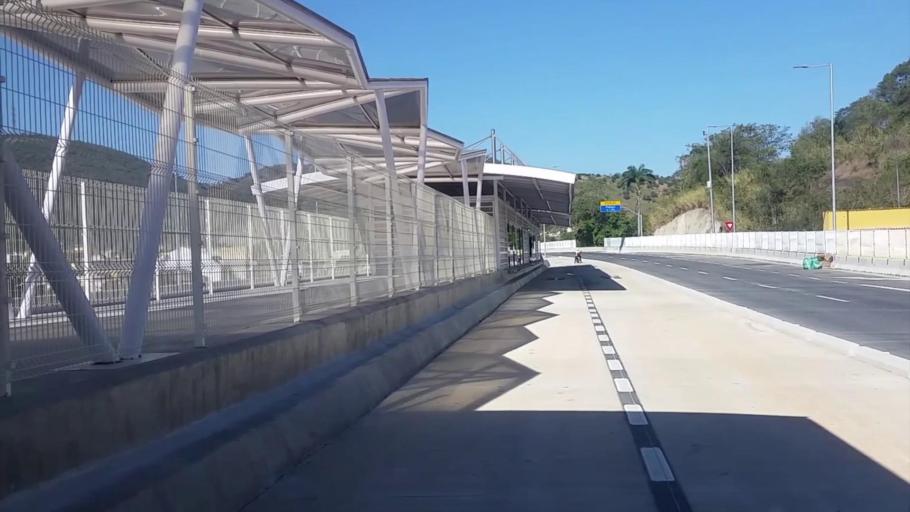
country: BR
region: Rio de Janeiro
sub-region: Nilopolis
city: Nilopolis
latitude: -22.8831
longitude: -43.4003
